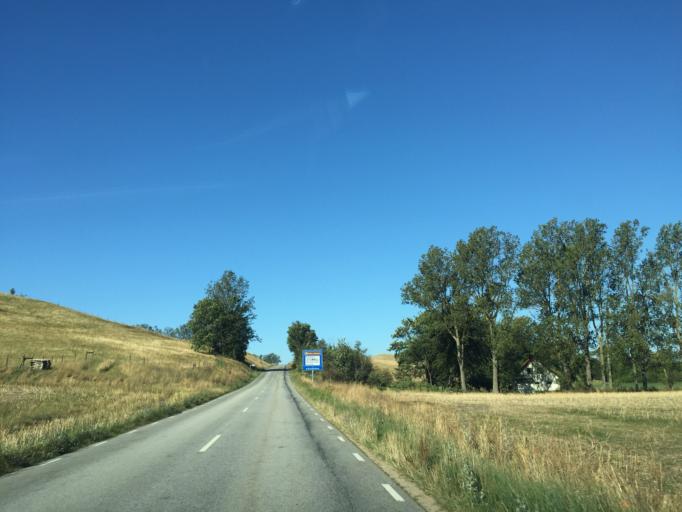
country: SE
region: Skane
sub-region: Ystads Kommun
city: Kopingebro
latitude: 55.3906
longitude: 14.0732
